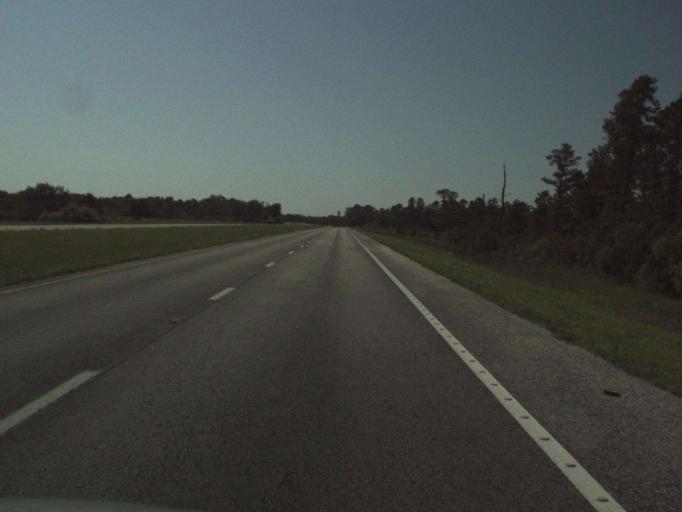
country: US
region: Florida
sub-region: Orange County
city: Wedgefield
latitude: 28.4964
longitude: -81.0464
